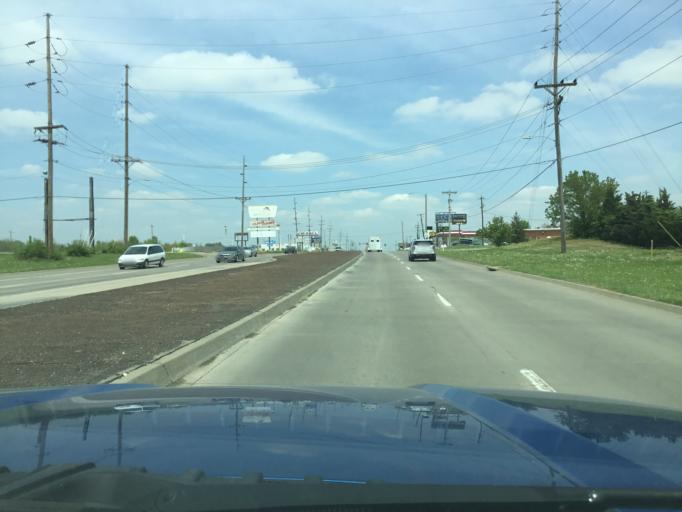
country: US
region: Kansas
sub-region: Shawnee County
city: Topeka
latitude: 38.9948
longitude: -95.6876
